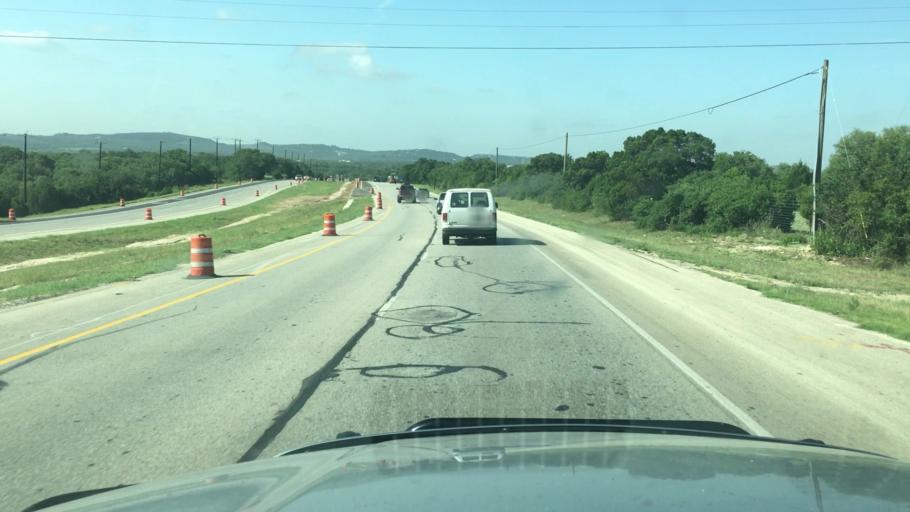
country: US
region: Texas
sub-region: Comal County
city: Bulverde
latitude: 29.7628
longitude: -98.4299
